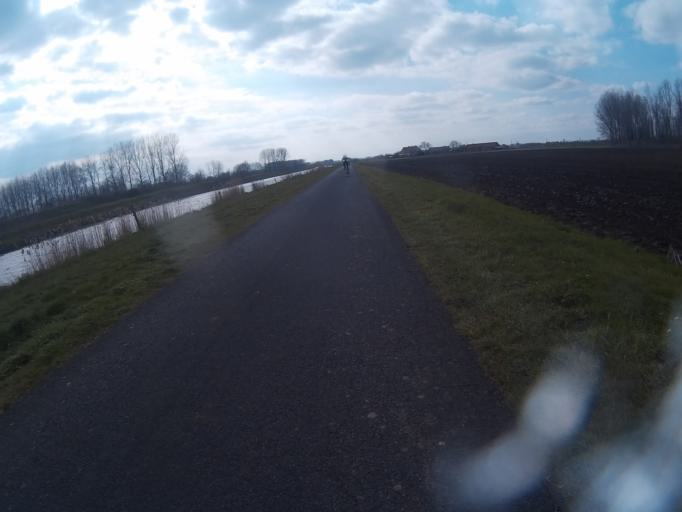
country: BE
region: Flanders
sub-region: Provincie Oost-Vlaanderen
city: Zomergem
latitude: 51.0942
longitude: 3.5536
